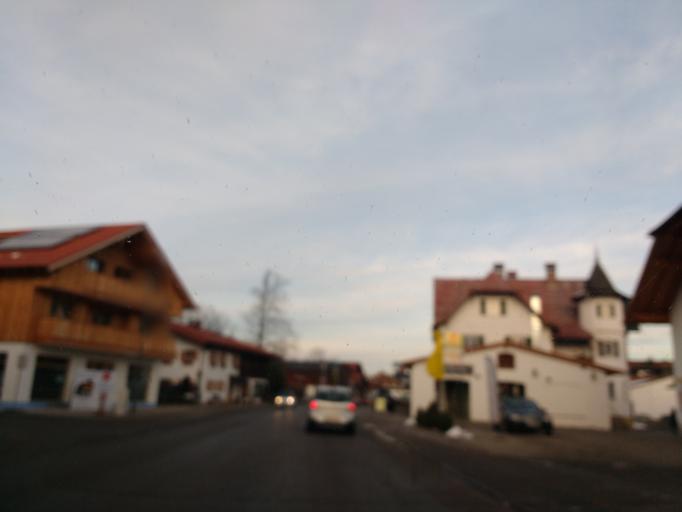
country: DE
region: Bavaria
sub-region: Swabia
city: Schwangau
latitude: 47.5755
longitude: 10.7352
